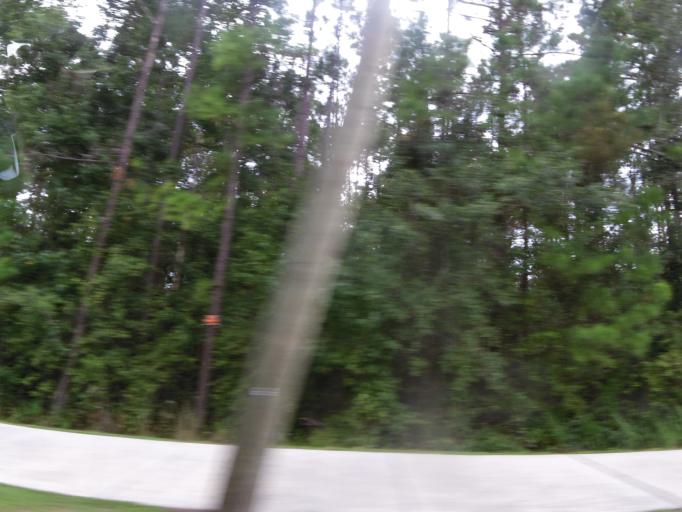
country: US
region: Florida
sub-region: Clay County
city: Asbury Lake
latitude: 30.0718
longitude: -81.8099
